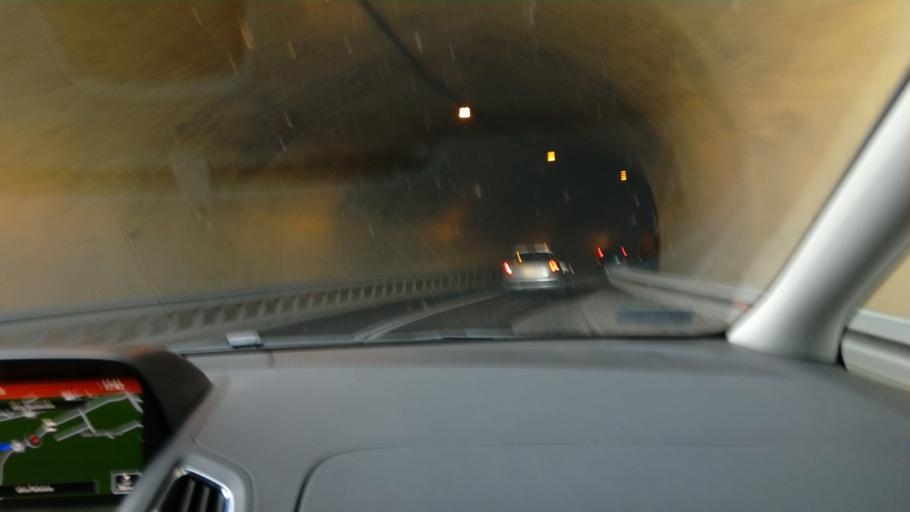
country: PL
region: Lower Silesian Voivodeship
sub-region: Powiat jeleniogorski
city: Karpacz
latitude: 50.7737
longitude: 15.7534
